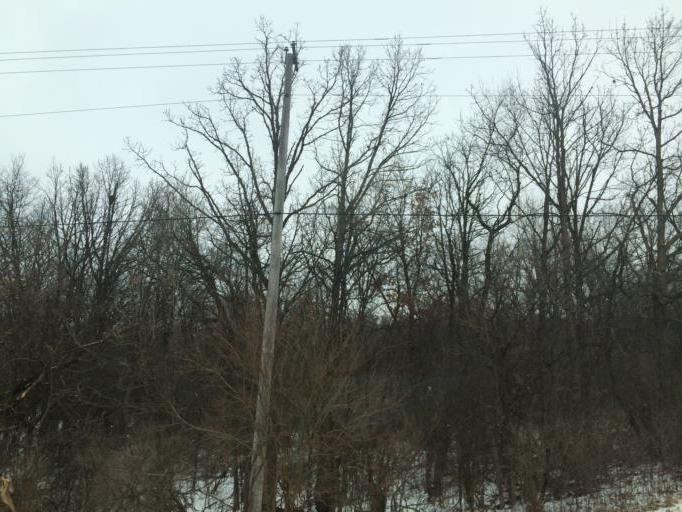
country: US
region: Illinois
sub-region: McHenry County
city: Harvard
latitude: 42.3606
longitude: -88.5606
